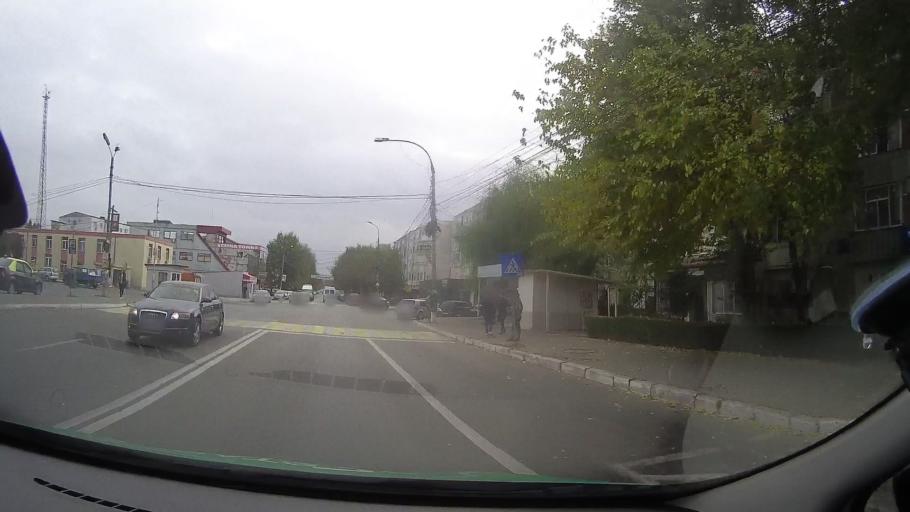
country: RO
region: Constanta
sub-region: Municipiul Medgidia
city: Medgidia
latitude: 44.2606
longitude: 28.2627
